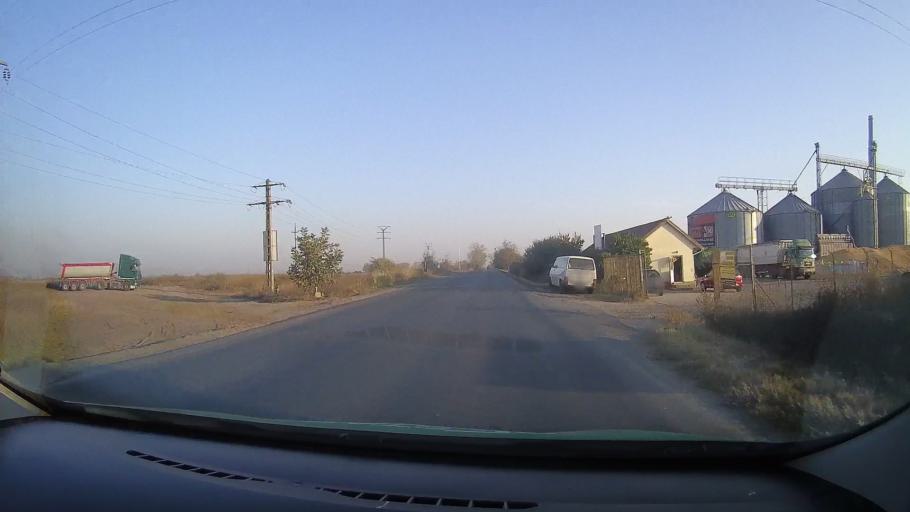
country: RO
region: Arad
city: Arad
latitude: 46.2194
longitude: 21.3205
